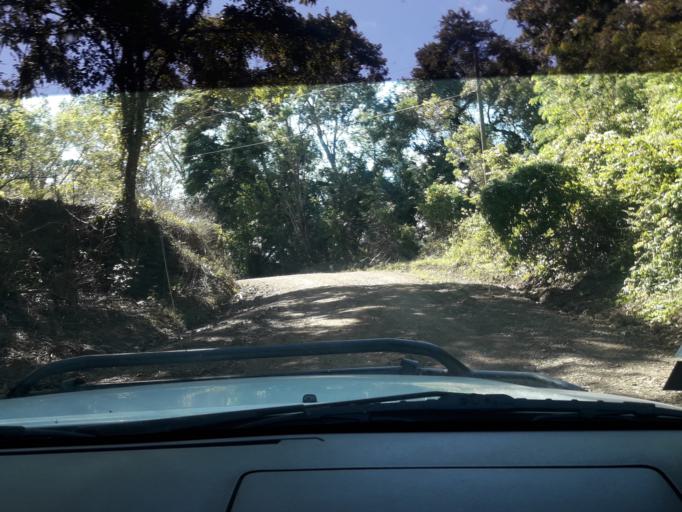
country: CR
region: Guanacaste
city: La Cruz
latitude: 11.1933
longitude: -85.6615
